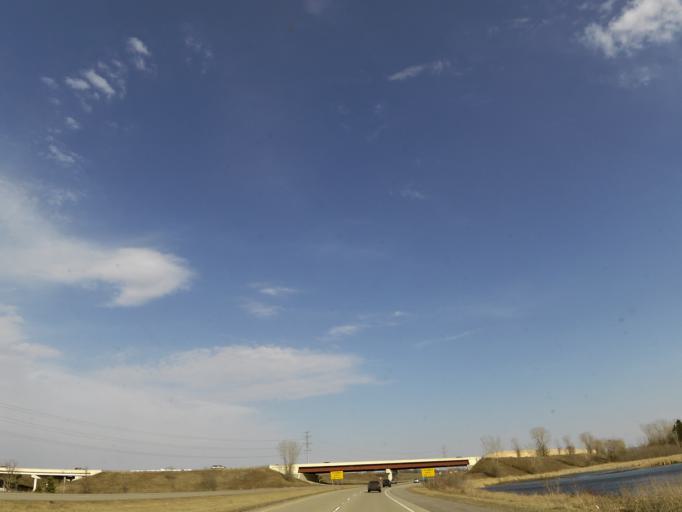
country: US
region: Minnesota
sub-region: Scott County
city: Savage
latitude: 44.7847
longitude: -93.4041
